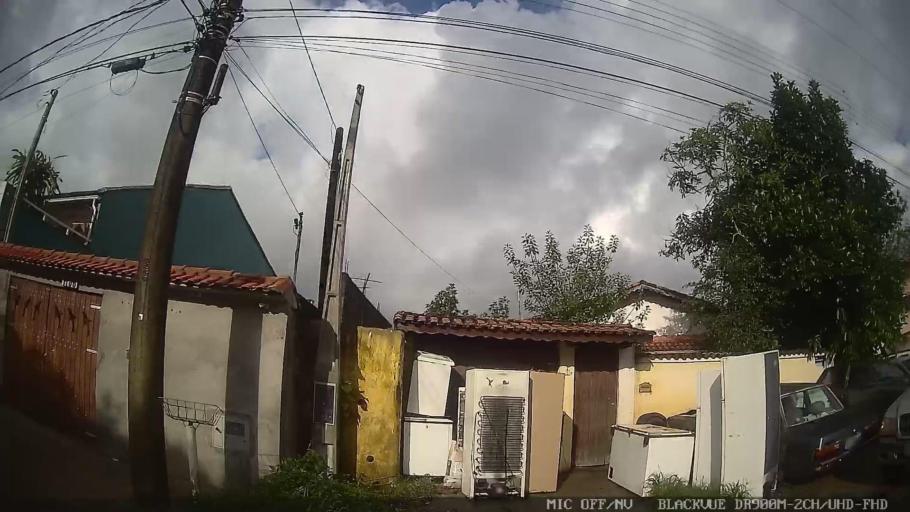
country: BR
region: Sao Paulo
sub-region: Itanhaem
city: Itanhaem
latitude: -24.2226
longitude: -46.8882
